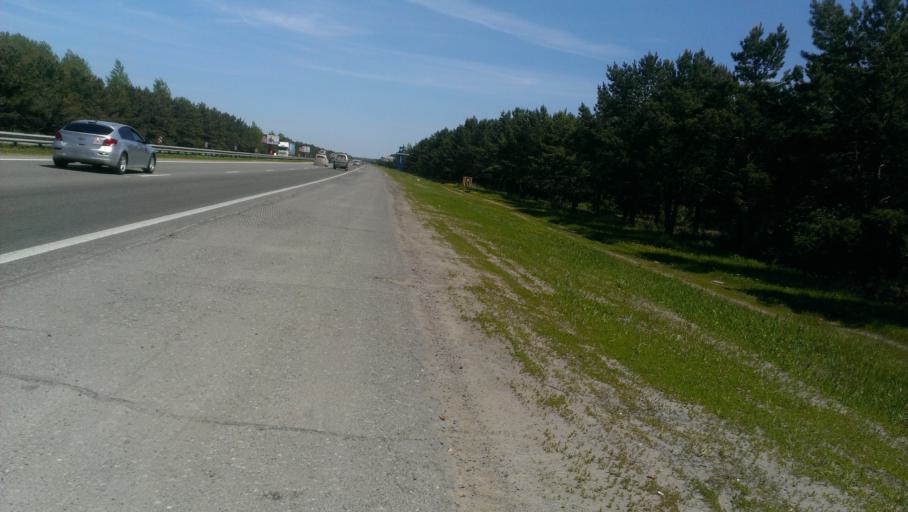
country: RU
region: Altai Krai
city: Zaton
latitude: 53.3162
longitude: 83.8665
